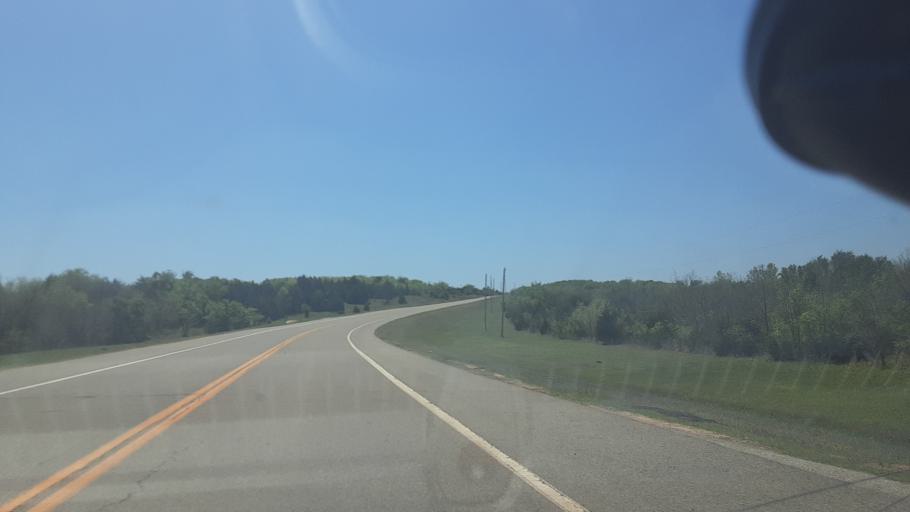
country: US
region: Oklahoma
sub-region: Logan County
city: Guthrie
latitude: 36.0497
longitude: -97.4070
